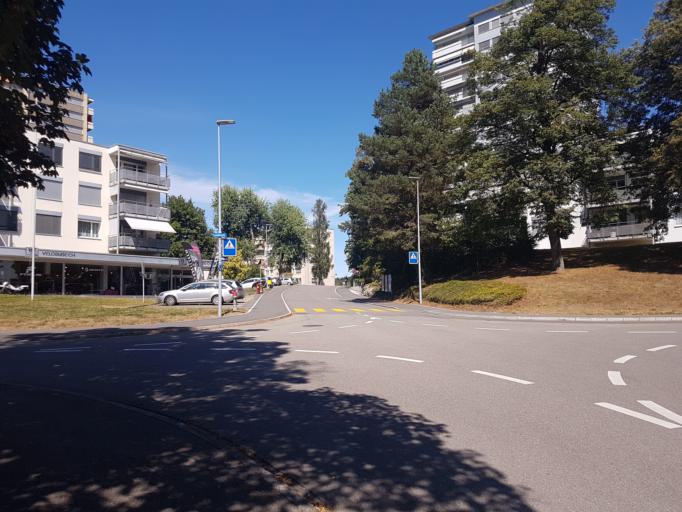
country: CH
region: Zurich
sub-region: Bezirk Pfaeffikon
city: Effretikon / Watt
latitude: 47.4291
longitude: 8.6962
